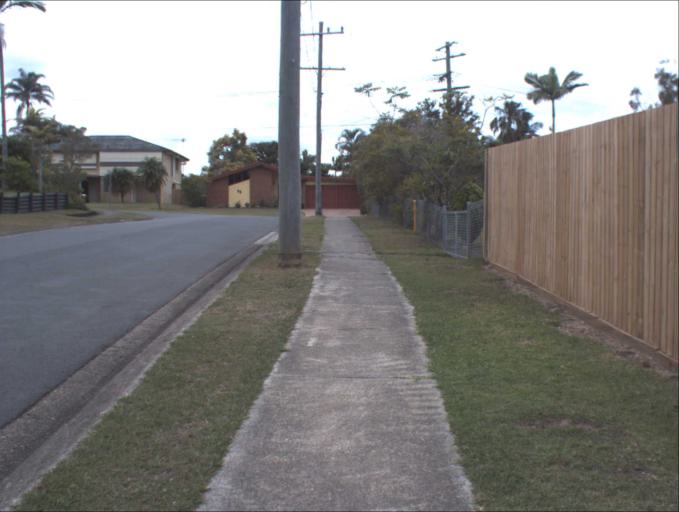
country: AU
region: Queensland
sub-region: Logan
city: Springwood
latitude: -27.6285
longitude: 153.1413
